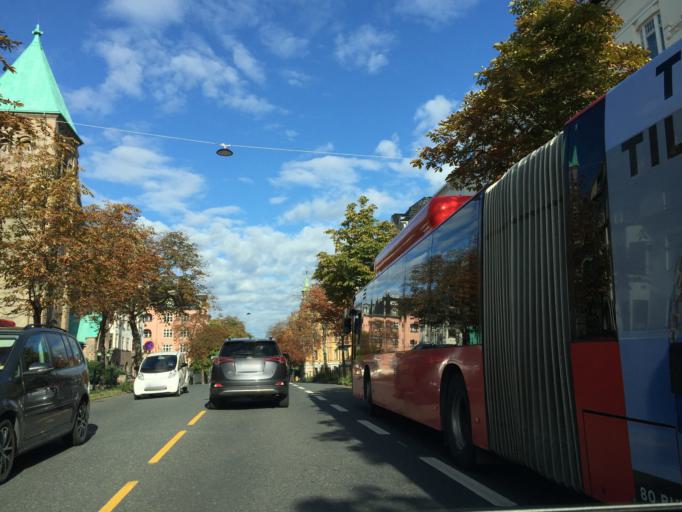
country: NO
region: Oslo
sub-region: Oslo
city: Sjolyststranda
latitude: 59.9175
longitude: 10.7082
